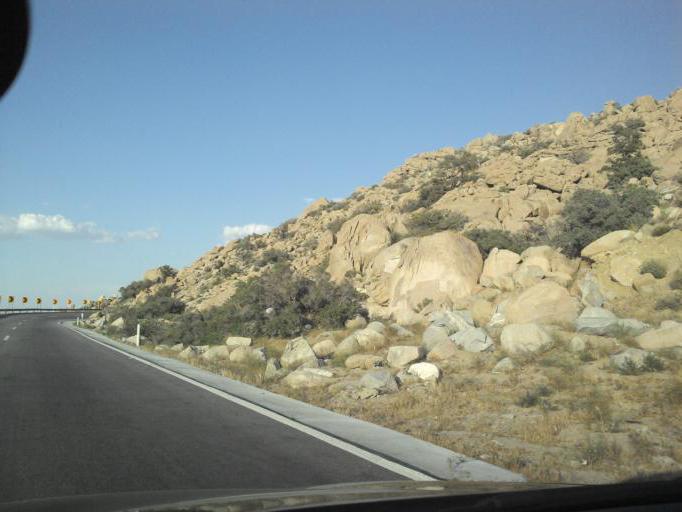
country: MX
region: Baja California
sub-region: Tecate
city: Cereso del Hongo
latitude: 32.5792
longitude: -116.0304
